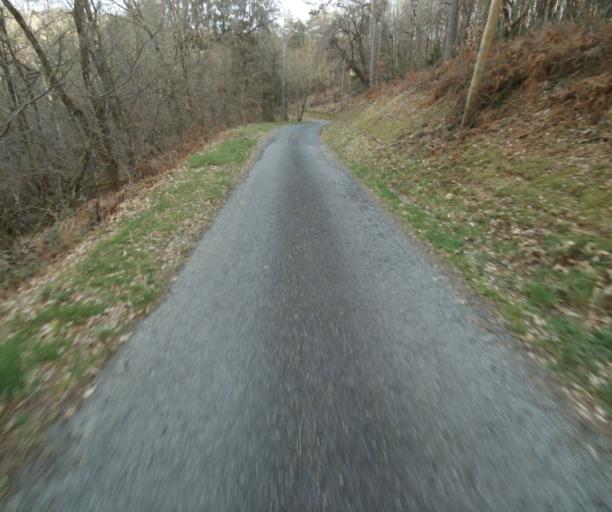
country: FR
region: Limousin
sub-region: Departement de la Correze
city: Correze
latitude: 45.3612
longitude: 1.8297
